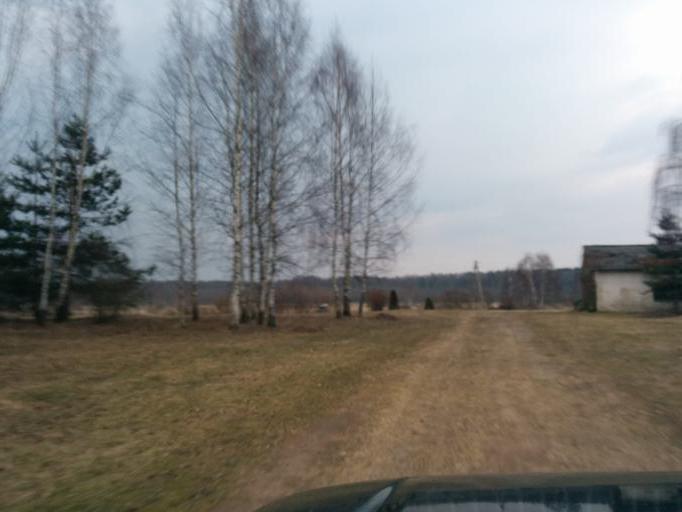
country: LV
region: Kekava
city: Kekava
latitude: 56.8007
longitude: 24.2777
